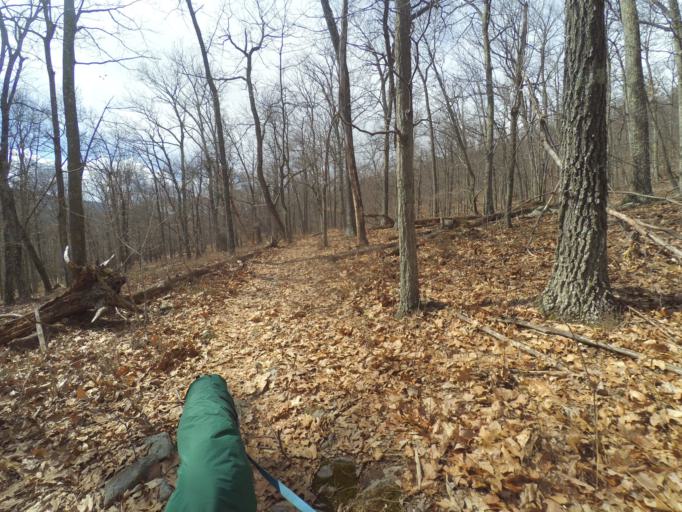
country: US
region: Pennsylvania
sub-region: Centre County
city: Centre Hall
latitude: 40.7652
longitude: -77.7054
